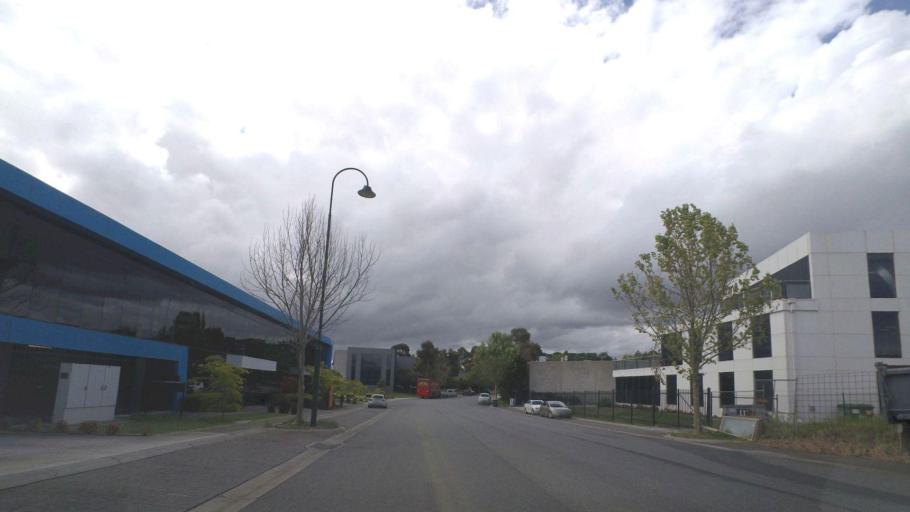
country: AU
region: Victoria
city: Forest Hill
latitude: -37.8316
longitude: 145.1893
